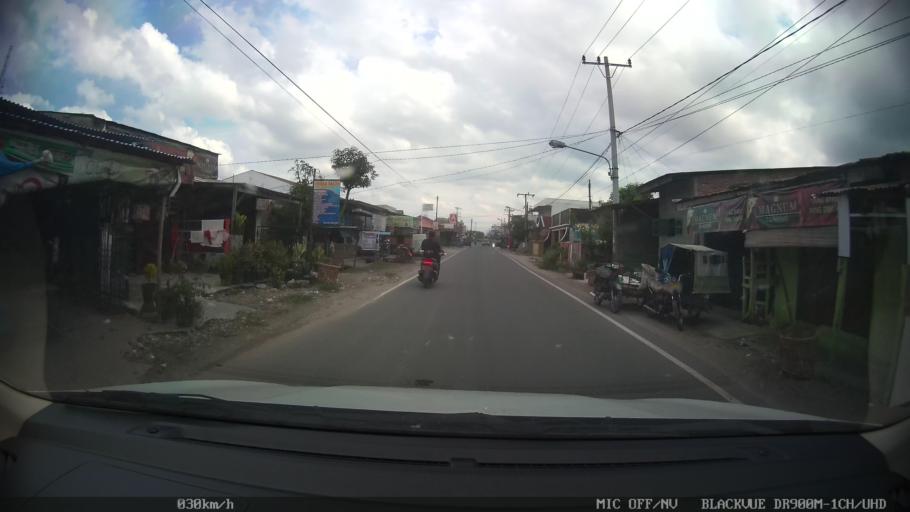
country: ID
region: North Sumatra
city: Sunggal
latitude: 3.6160
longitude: 98.6240
